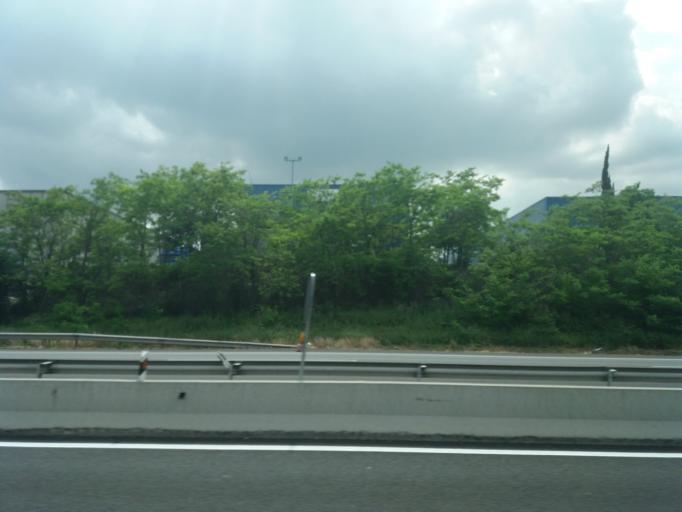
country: ES
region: Catalonia
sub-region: Provincia de Barcelona
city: Abrera
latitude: 41.5115
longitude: 1.9007
